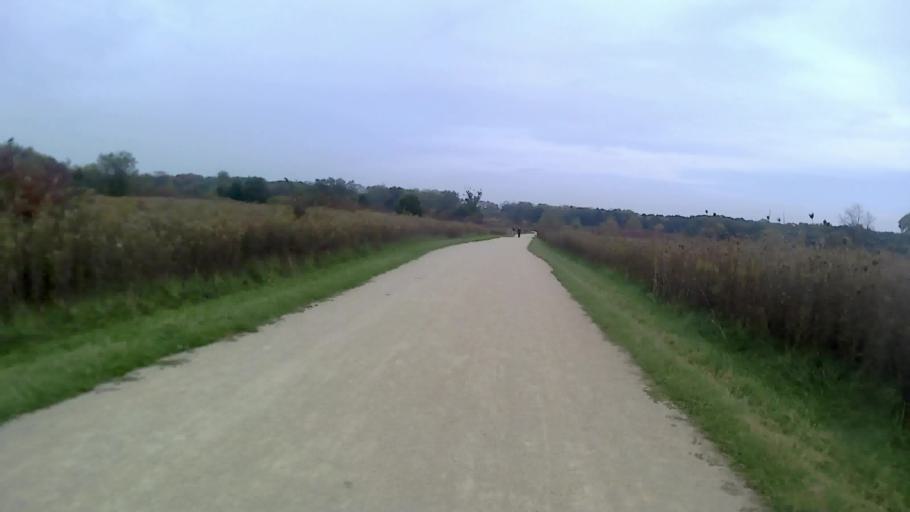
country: US
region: Illinois
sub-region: DuPage County
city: Warrenville
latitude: 41.8176
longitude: -88.1452
